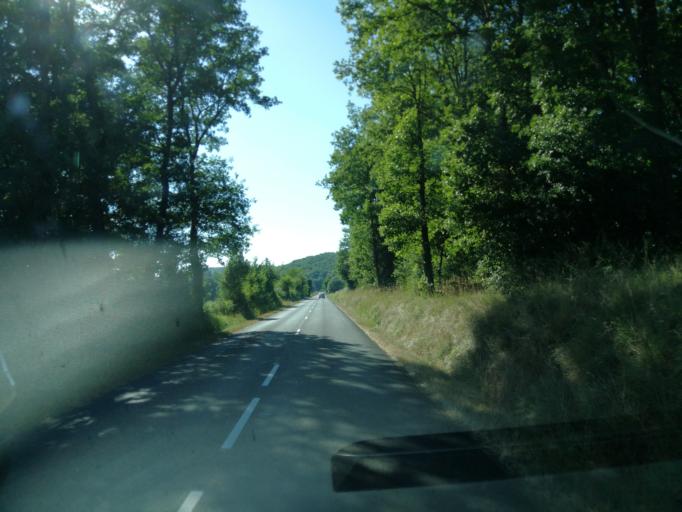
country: FR
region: Midi-Pyrenees
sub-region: Departement du Lot
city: Gourdon
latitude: 44.7078
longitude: 1.3391
